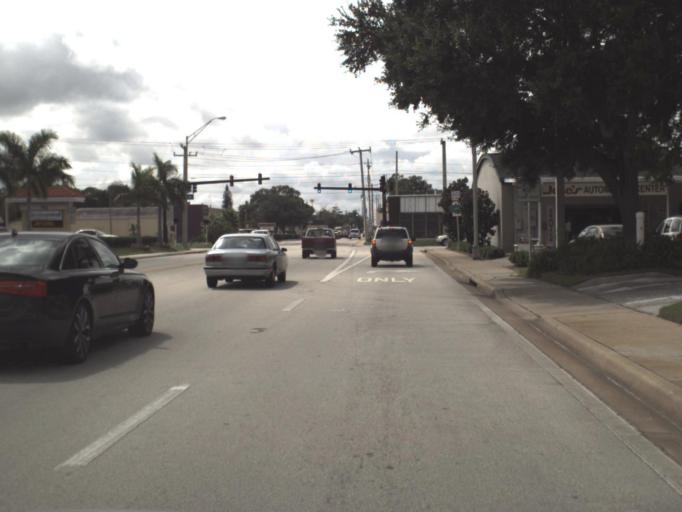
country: US
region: Florida
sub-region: Manatee County
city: Bradenton
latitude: 27.4938
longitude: -82.5713
